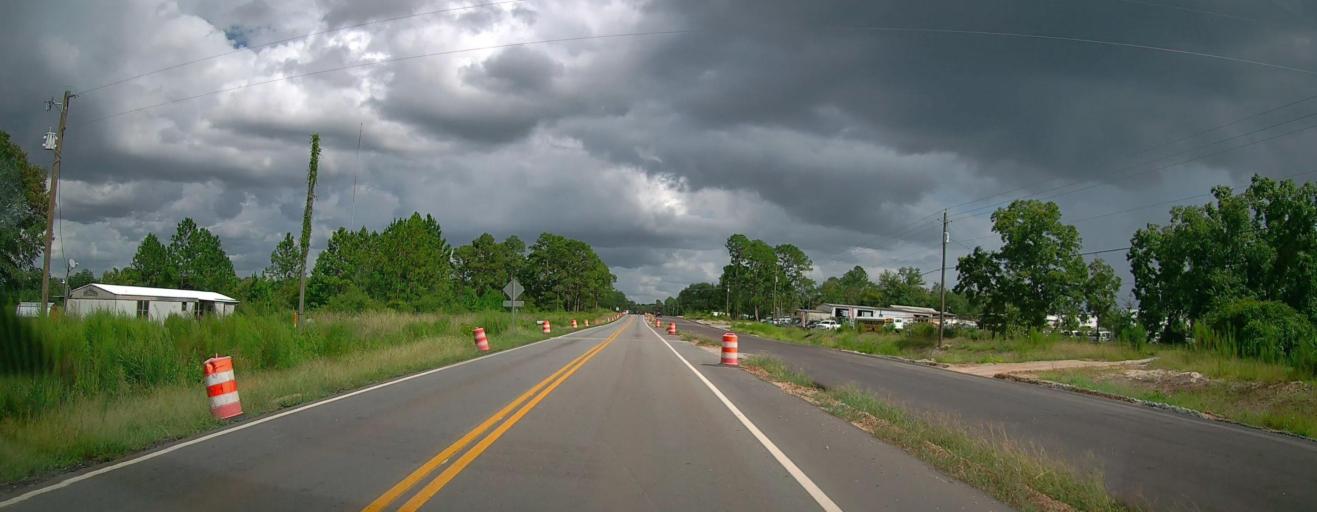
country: US
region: Georgia
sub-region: Coffee County
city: Douglas
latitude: 31.5323
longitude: -82.9137
